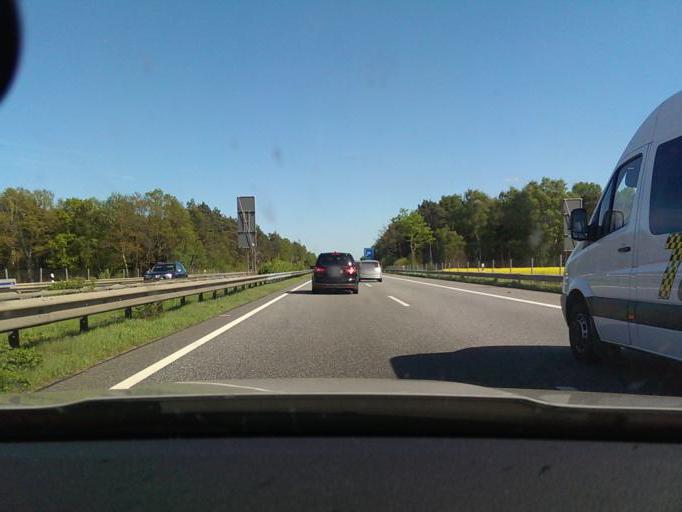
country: DE
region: Lower Saxony
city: Langwedel
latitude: 53.0078
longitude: 9.1578
